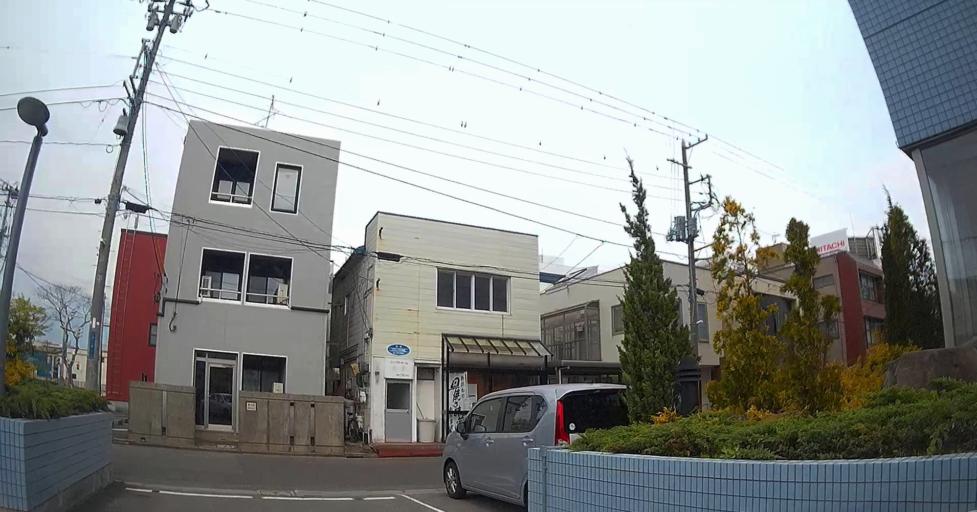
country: JP
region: Aomori
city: Aomori Shi
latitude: 40.8218
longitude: 140.7459
